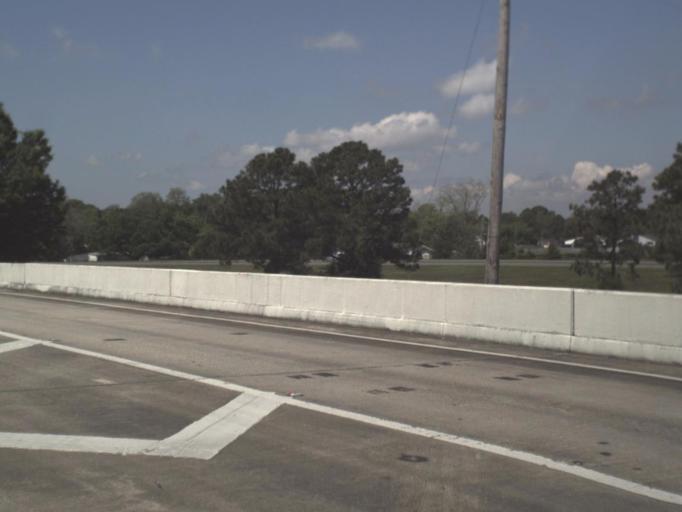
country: US
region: Florida
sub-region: Escambia County
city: West Pensacola
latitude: 30.4309
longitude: -87.2727
